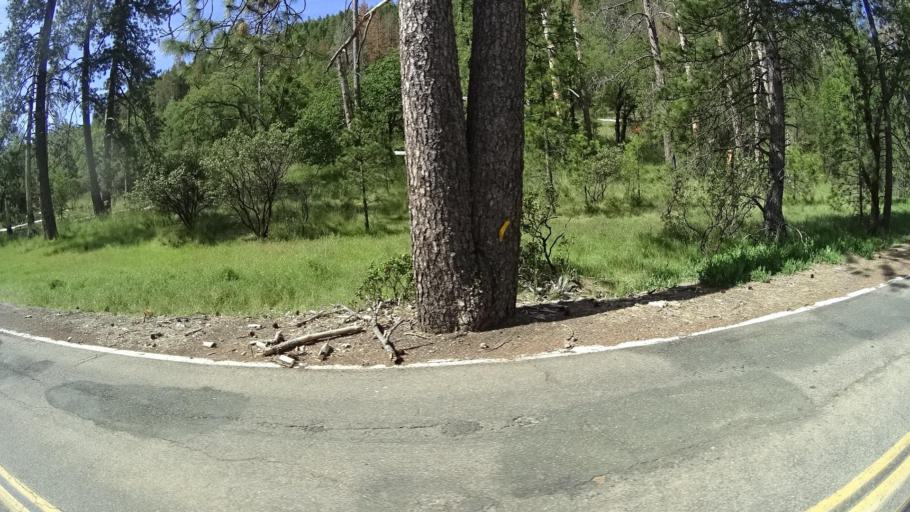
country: US
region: California
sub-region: Lake County
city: Cobb
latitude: 38.8548
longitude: -122.7324
